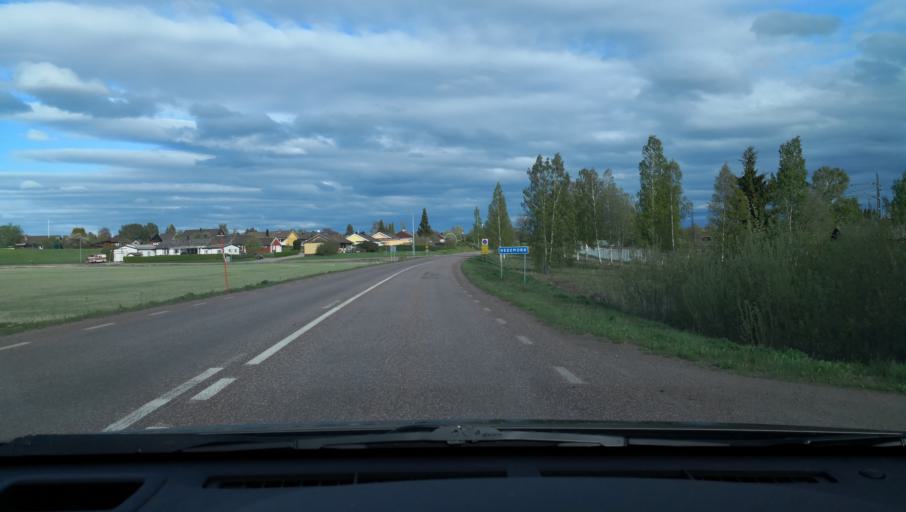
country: SE
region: Dalarna
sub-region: Hedemora Kommun
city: Hedemora
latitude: 60.2819
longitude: 15.9606
